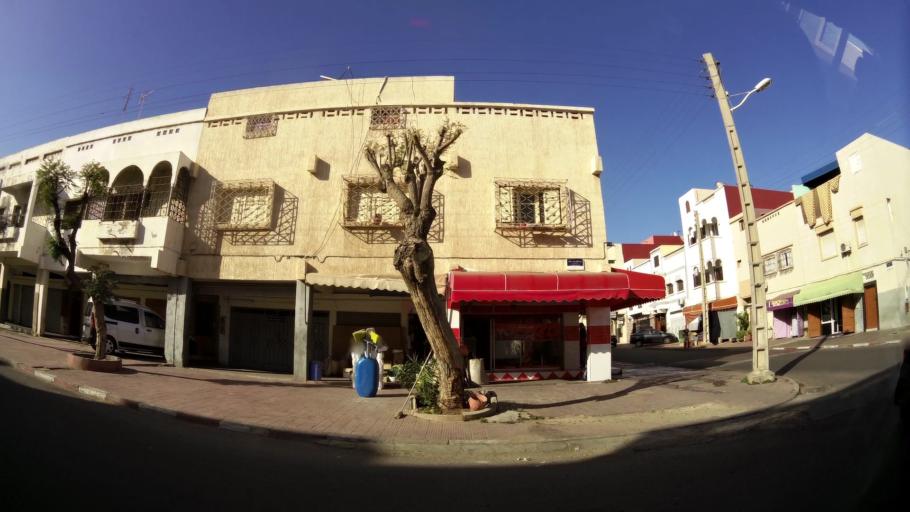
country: MA
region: Souss-Massa-Draa
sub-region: Agadir-Ida-ou-Tnan
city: Agadir
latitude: 30.4296
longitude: -9.5779
